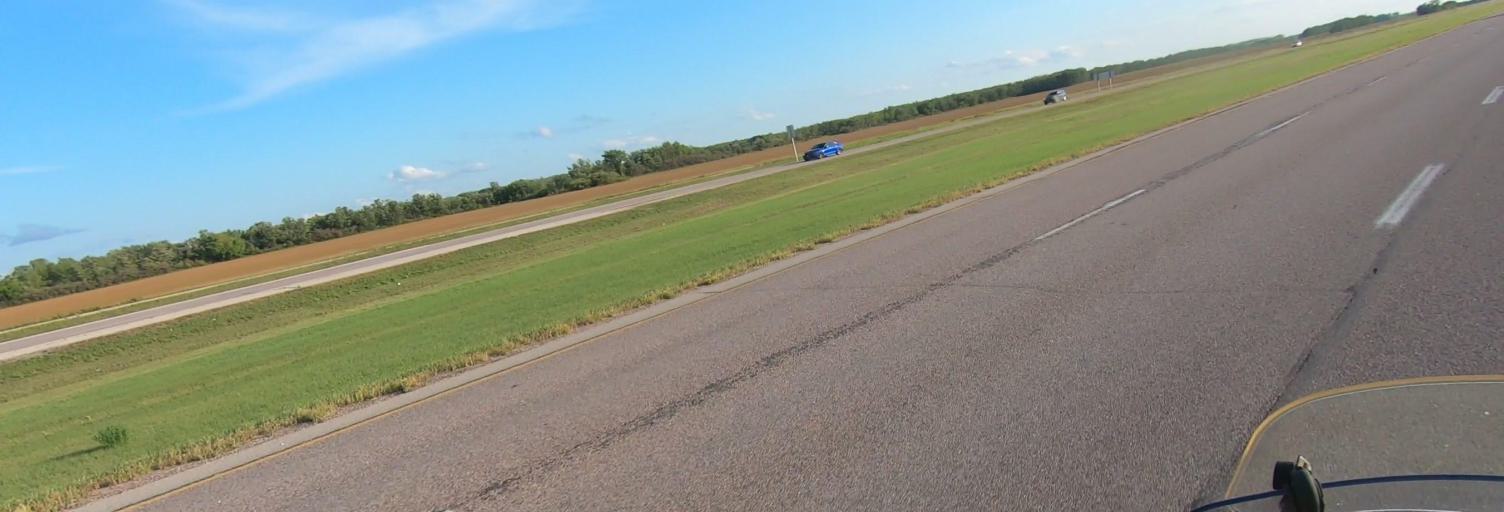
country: CA
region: Manitoba
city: Selkirk
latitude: 50.1134
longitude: -96.8429
